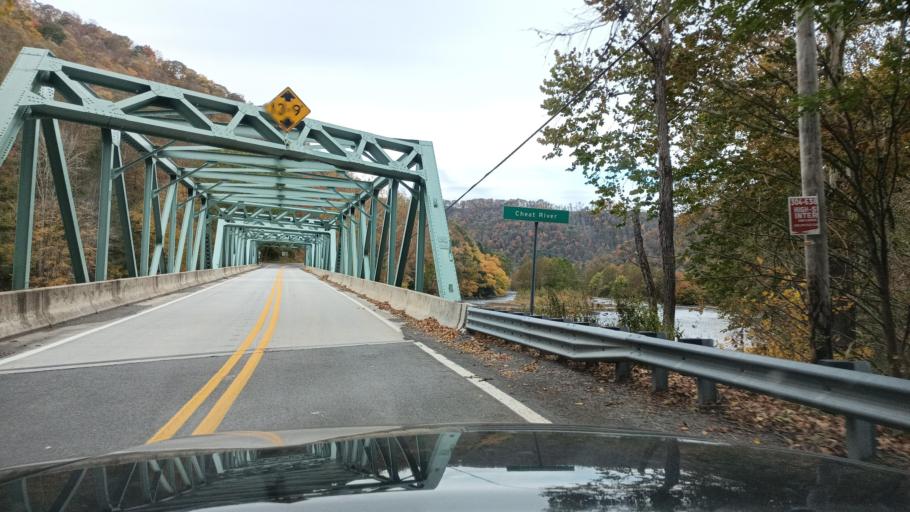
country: US
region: West Virginia
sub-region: Preston County
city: Kingwood
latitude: 39.3198
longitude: -79.6563
